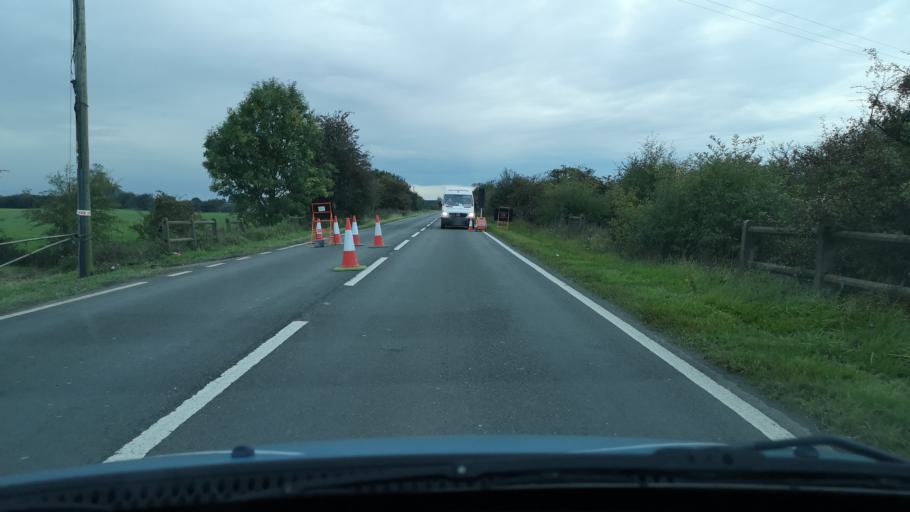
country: GB
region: England
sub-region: Doncaster
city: Hatfield
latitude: 53.5933
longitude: -0.9505
